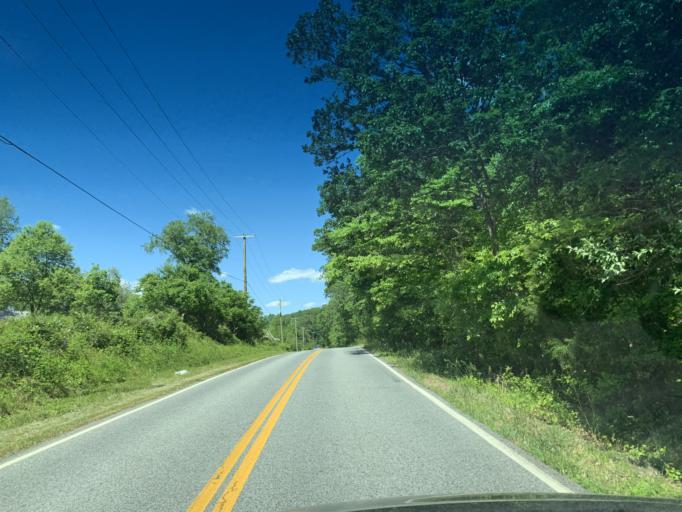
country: US
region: Maryland
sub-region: Cecil County
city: North East
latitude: 39.5456
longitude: -75.9125
